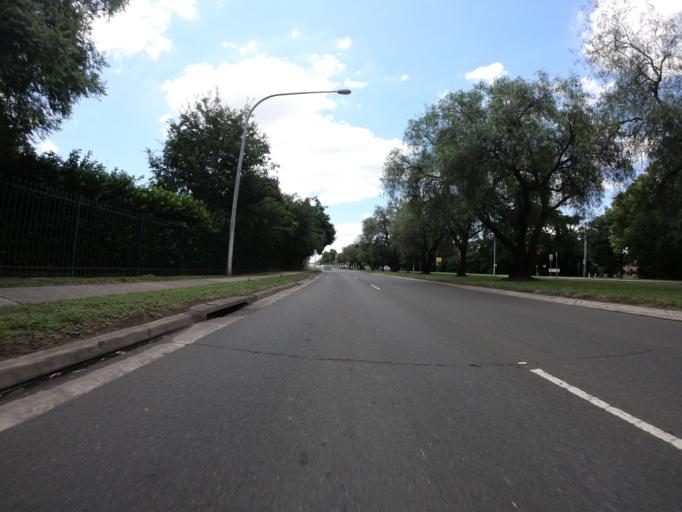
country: AU
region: New South Wales
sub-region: Penrith Municipality
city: Penrith
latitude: -33.7551
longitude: 150.6869
